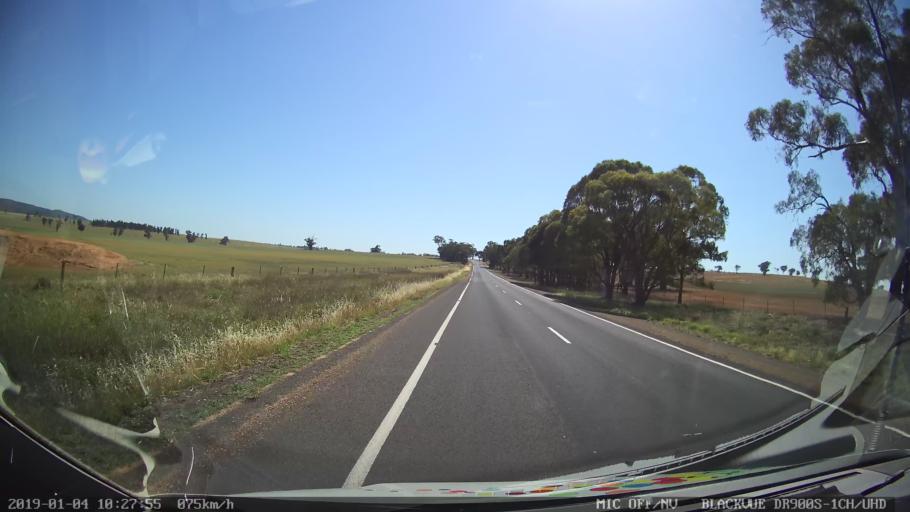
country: AU
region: New South Wales
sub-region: Cabonne
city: Canowindra
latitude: -33.3663
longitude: 148.6036
